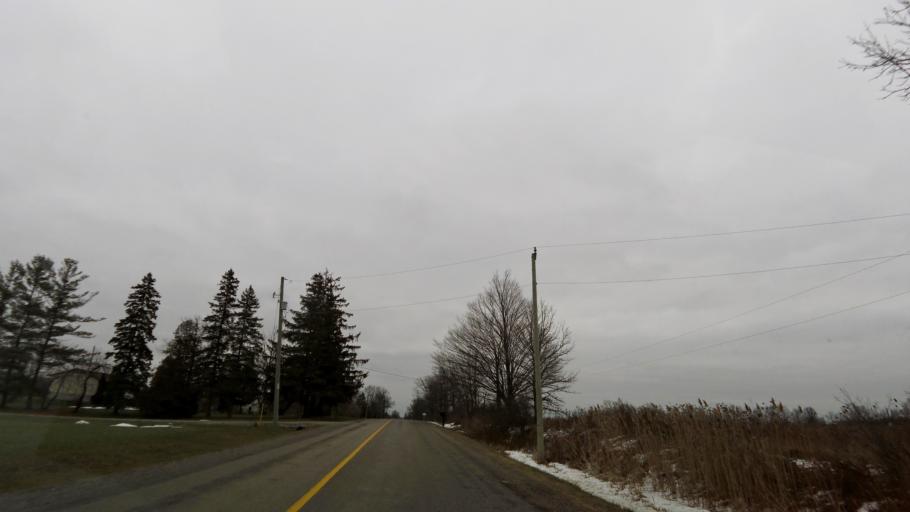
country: CA
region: Ontario
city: Ancaster
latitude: 43.0117
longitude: -80.0753
